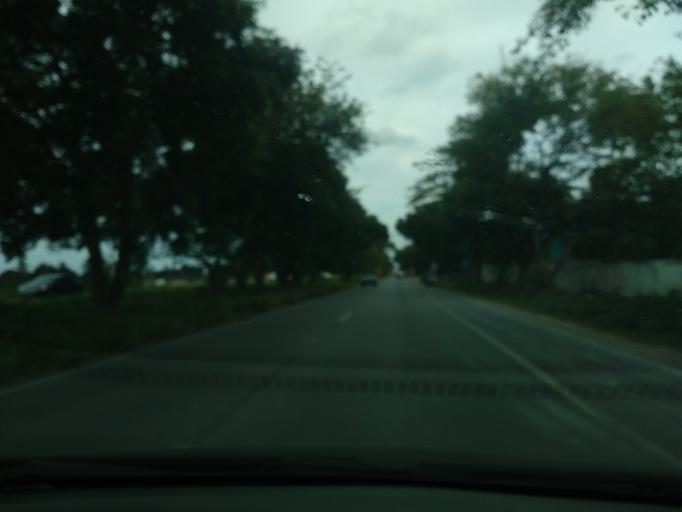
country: BR
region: Alagoas
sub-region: Rio Largo
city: Rio Largo
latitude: -9.4939
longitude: -35.8140
